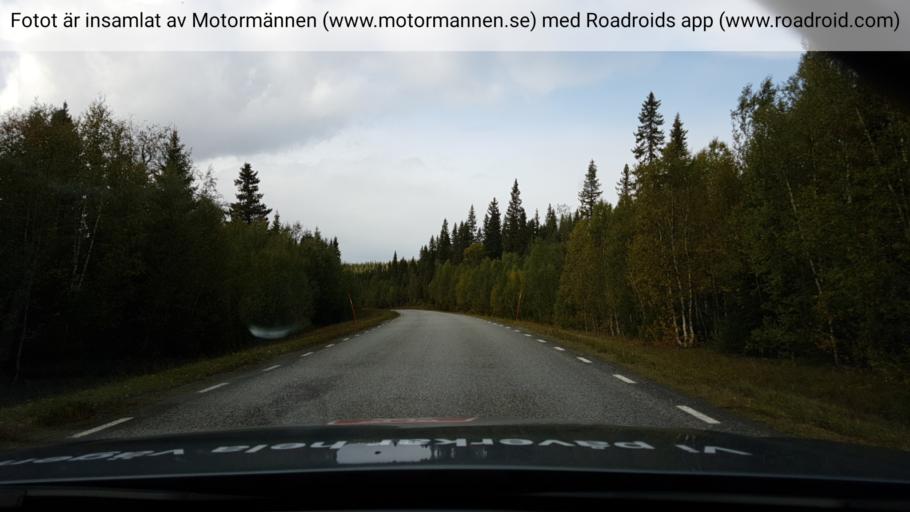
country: SE
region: Jaemtland
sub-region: Are Kommun
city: Are
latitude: 63.7386
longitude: 13.0484
